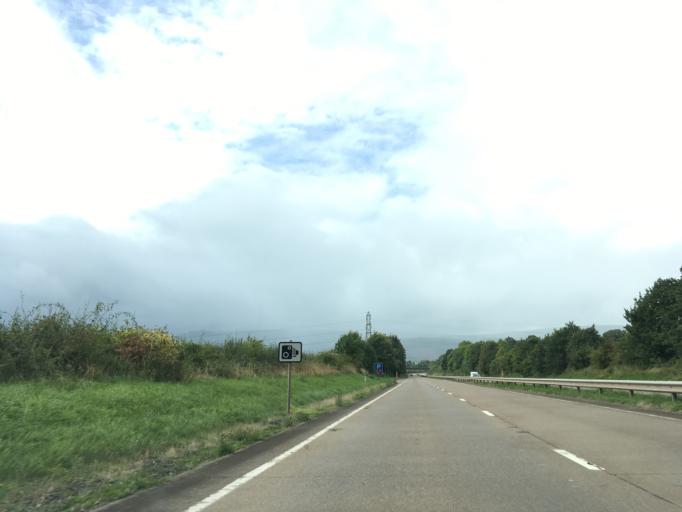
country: GB
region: Wales
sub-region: Monmouthshire
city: Llanarth
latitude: 51.7844
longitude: -2.9620
